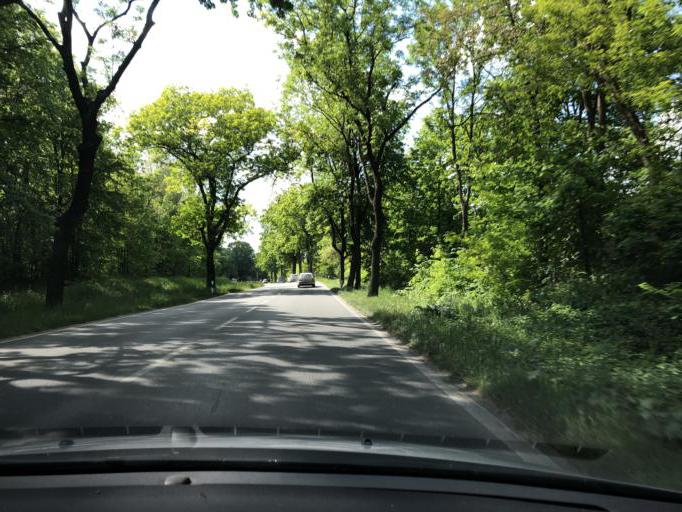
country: DE
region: Brandenburg
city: Petershagen
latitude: 52.4869
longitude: 13.8203
